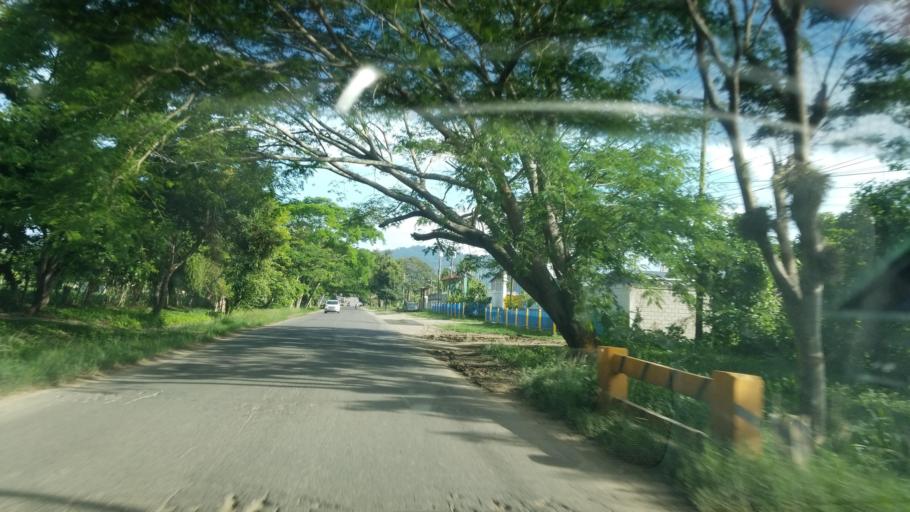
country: HN
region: El Paraiso
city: Cuyali
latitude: 13.8910
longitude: -86.5550
